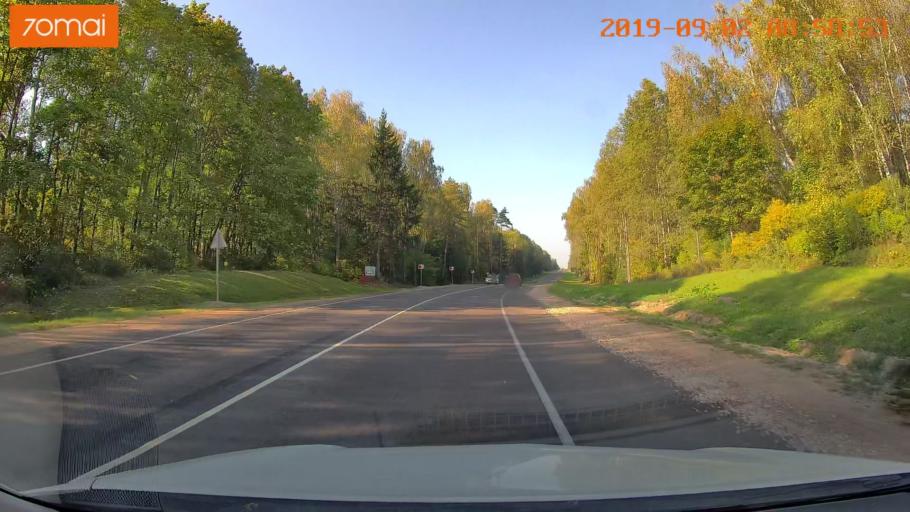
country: RU
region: Kaluga
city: Myatlevo
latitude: 54.9252
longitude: 35.7430
